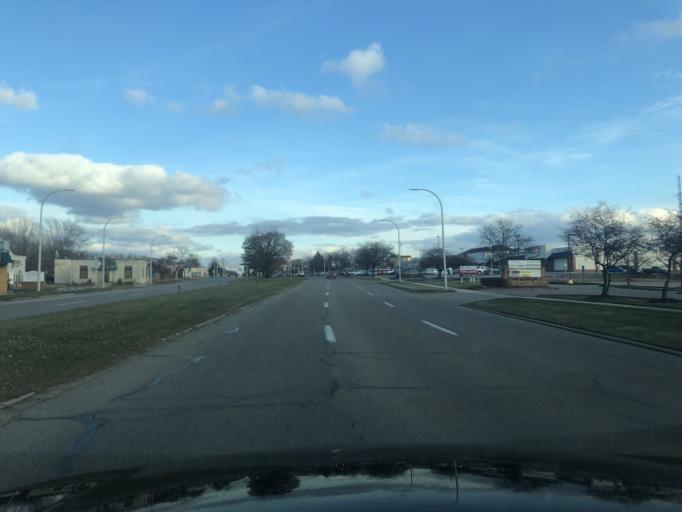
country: US
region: Michigan
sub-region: Wayne County
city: Livonia
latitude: 42.3971
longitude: -83.3774
